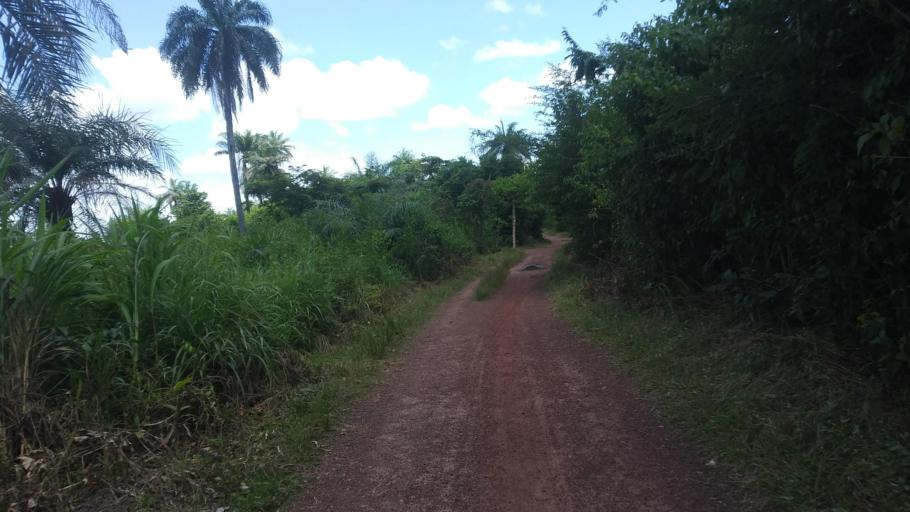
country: SL
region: Northern Province
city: Makeni
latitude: 8.8988
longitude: -11.9954
